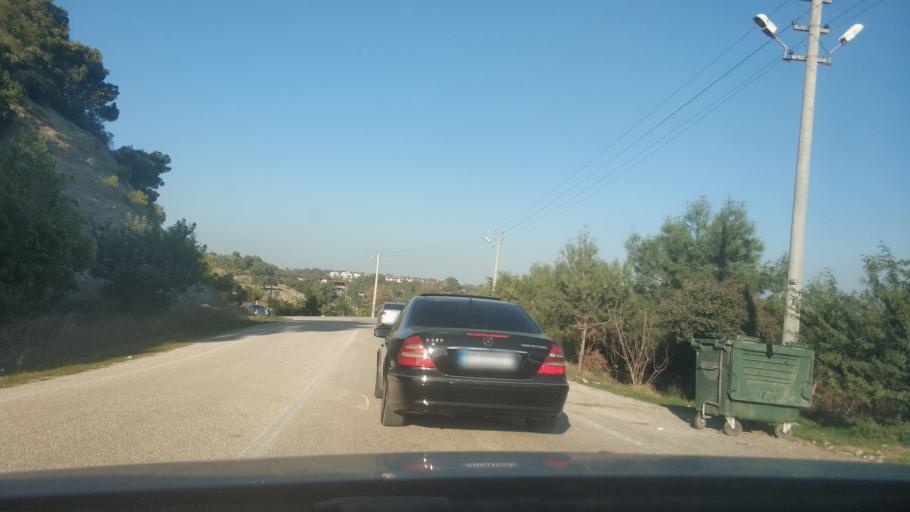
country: TR
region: Adana
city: Adana
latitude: 37.0997
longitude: 35.2905
